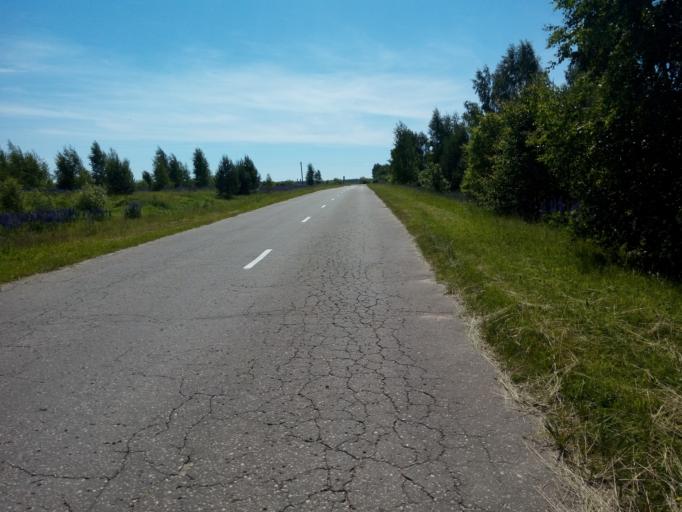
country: RU
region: Nizjnij Novgorod
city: Voskresenskoye
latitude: 56.7701
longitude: 45.5531
